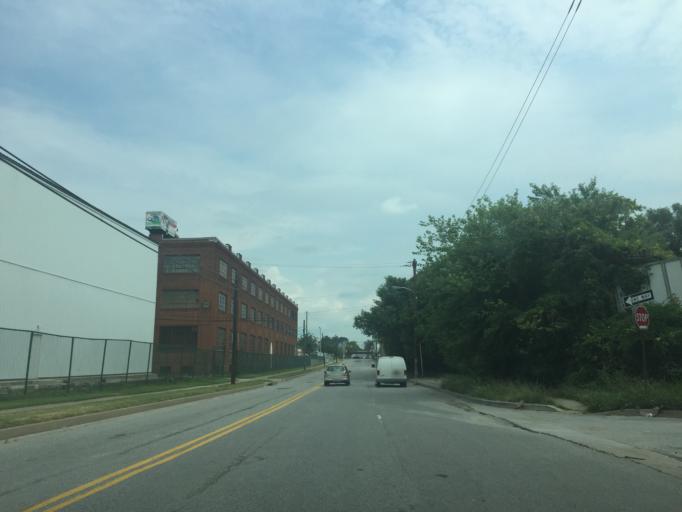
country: US
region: Maryland
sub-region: Baltimore County
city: Rosedale
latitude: 39.2954
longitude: -76.5601
